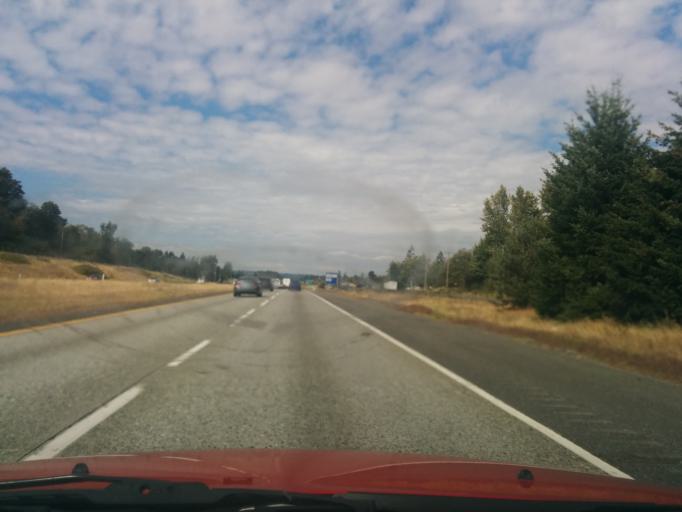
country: US
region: Washington
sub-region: Whatcom County
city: Marietta-Alderwood
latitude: 48.8098
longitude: -122.5407
